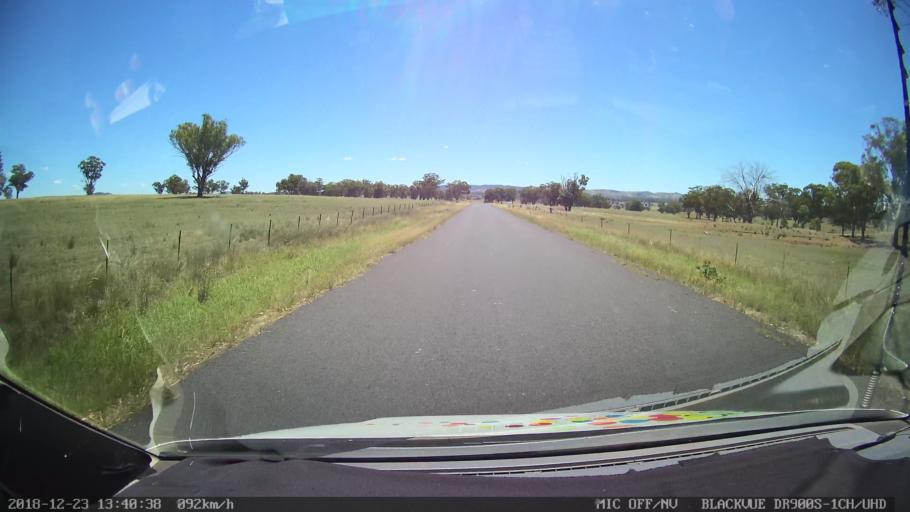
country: AU
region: New South Wales
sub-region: Armidale Dumaresq
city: Armidale
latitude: -30.4671
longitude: 151.1881
